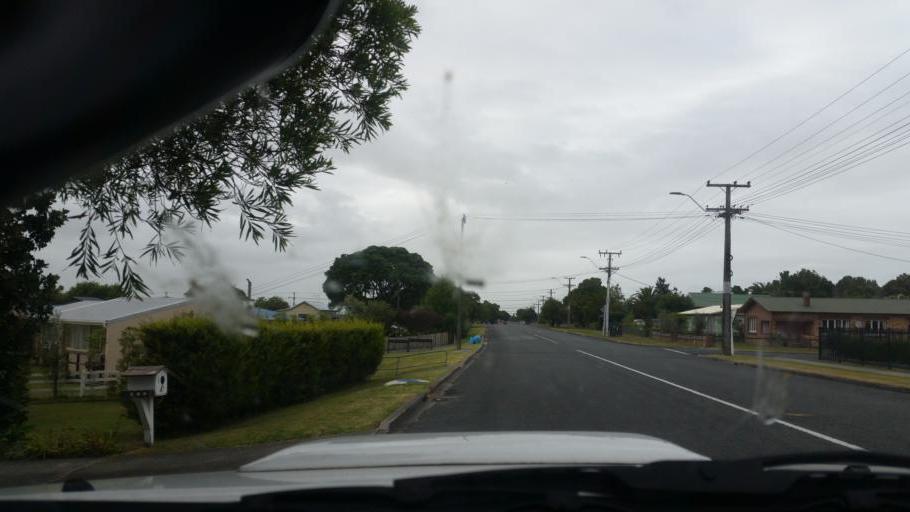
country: NZ
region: Northland
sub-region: Kaipara District
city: Dargaville
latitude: -35.9332
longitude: 173.8723
